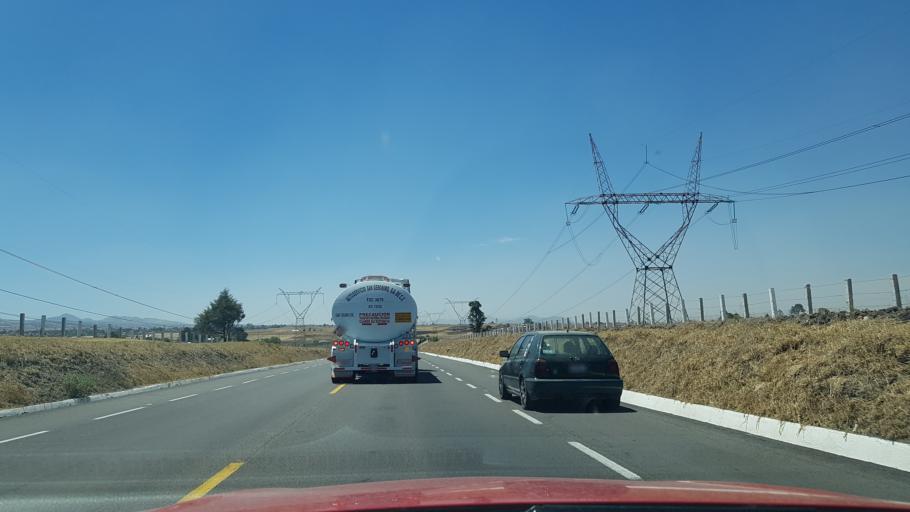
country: MX
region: Mexico
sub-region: Almoloya de Juarez
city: Villa de Almoloya de Juarez
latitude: 19.3850
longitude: -99.7629
